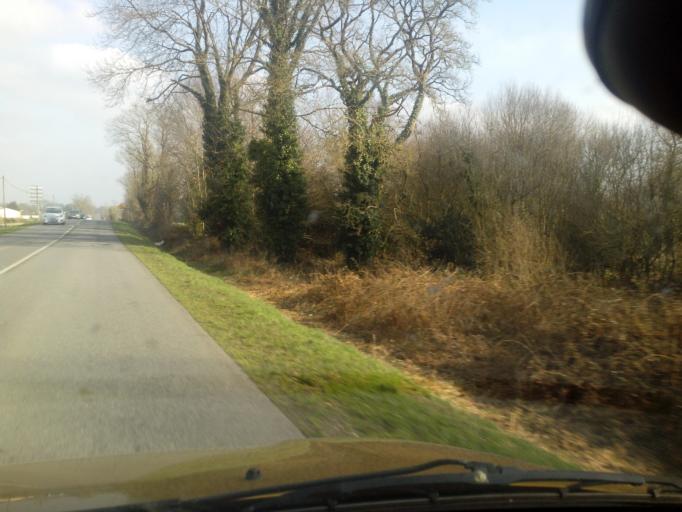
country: FR
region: Brittany
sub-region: Departement du Morbihan
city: La Vraie-Croix
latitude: 47.6959
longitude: -2.5050
